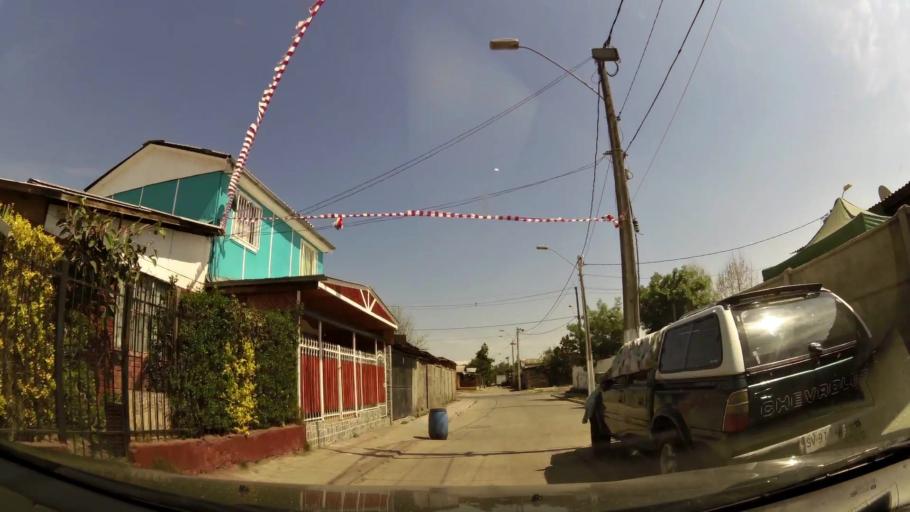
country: CL
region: Santiago Metropolitan
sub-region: Provincia de Santiago
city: La Pintana
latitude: -33.5886
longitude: -70.6121
